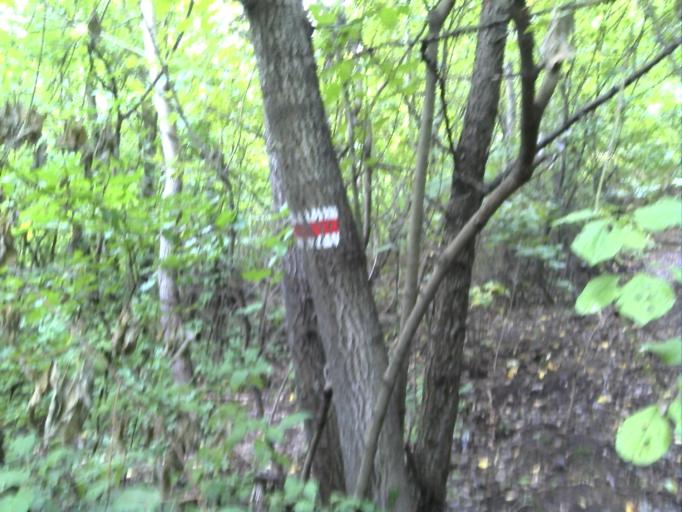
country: HU
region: Borsod-Abauj-Zemplen
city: Satoraljaujhely
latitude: 48.4062
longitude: 21.6389
